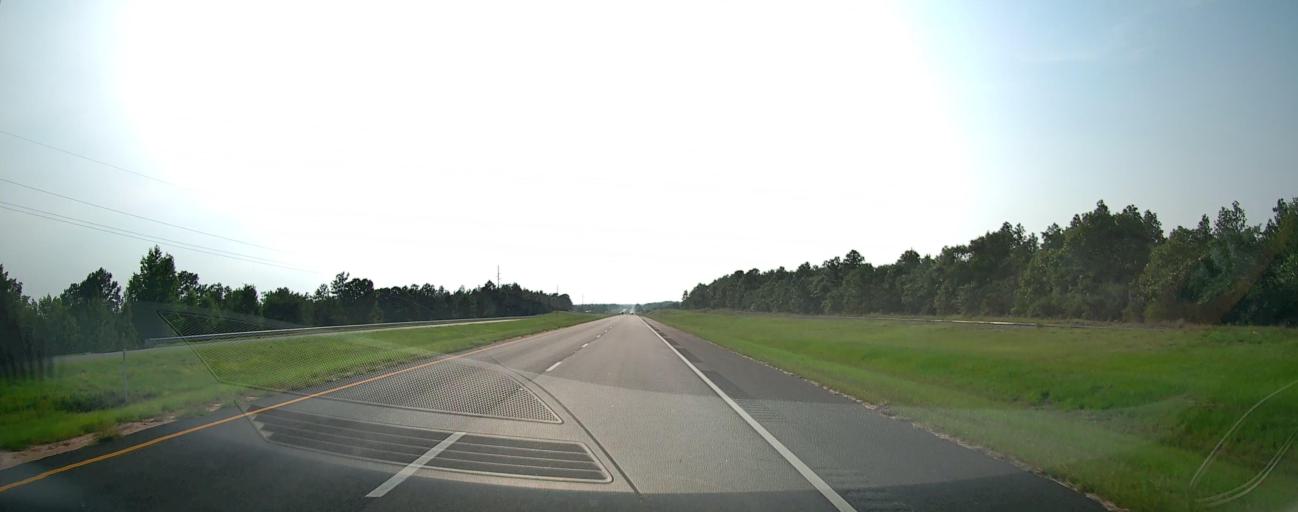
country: US
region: Georgia
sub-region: Taylor County
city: Butler
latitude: 32.5808
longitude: -84.3233
